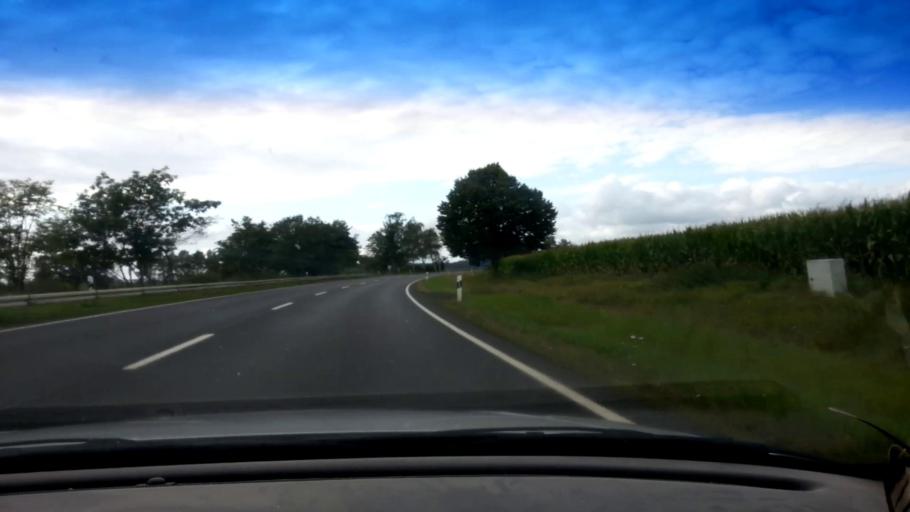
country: DE
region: Bavaria
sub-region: Upper Palatinate
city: Pechbrunn
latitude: 49.9757
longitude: 12.1381
